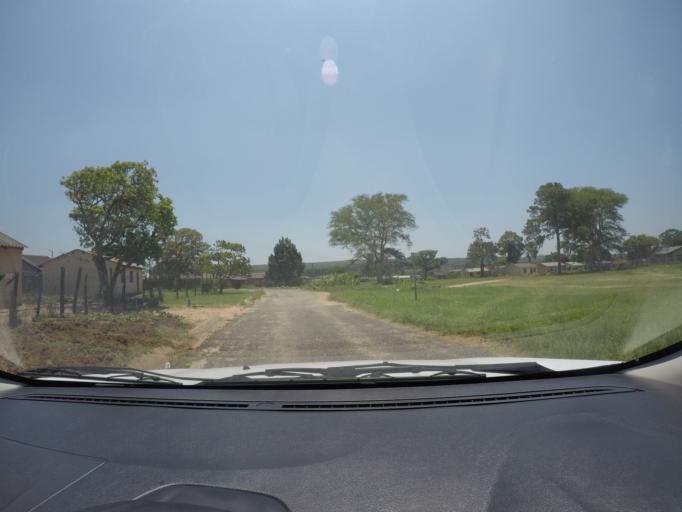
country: ZA
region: KwaZulu-Natal
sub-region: uThungulu District Municipality
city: eSikhawini
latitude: -28.8819
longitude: 31.8928
